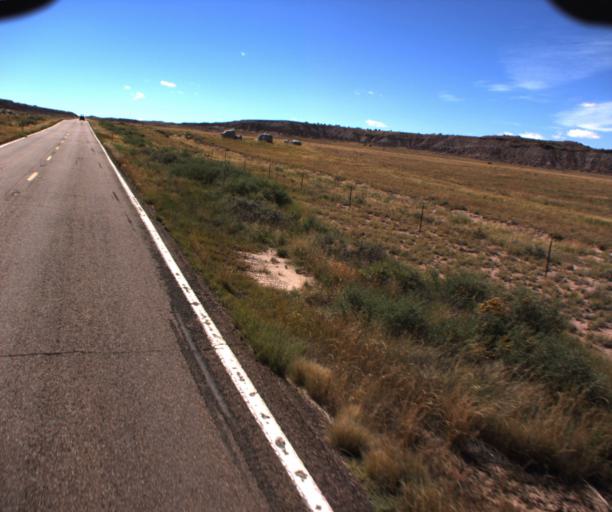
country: US
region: Arizona
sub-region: Apache County
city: Saint Johns
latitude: 34.6687
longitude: -109.2892
